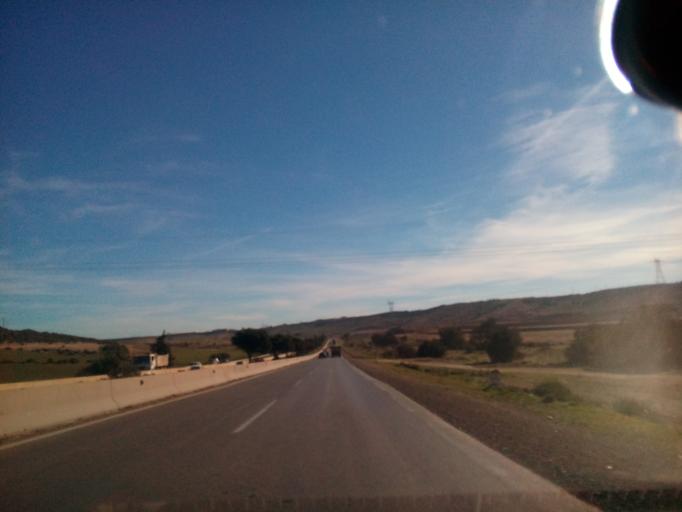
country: DZ
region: Oran
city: Ain el Bya
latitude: 35.7706
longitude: -0.2404
